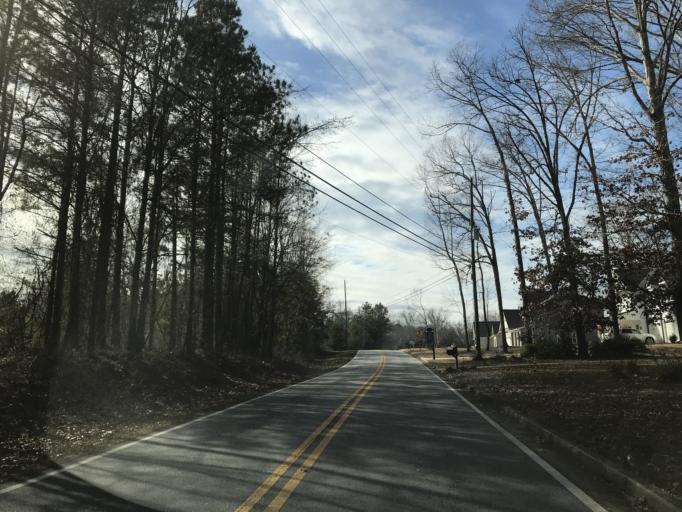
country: US
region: Georgia
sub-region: Douglas County
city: Douglasville
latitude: 33.7969
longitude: -84.8101
